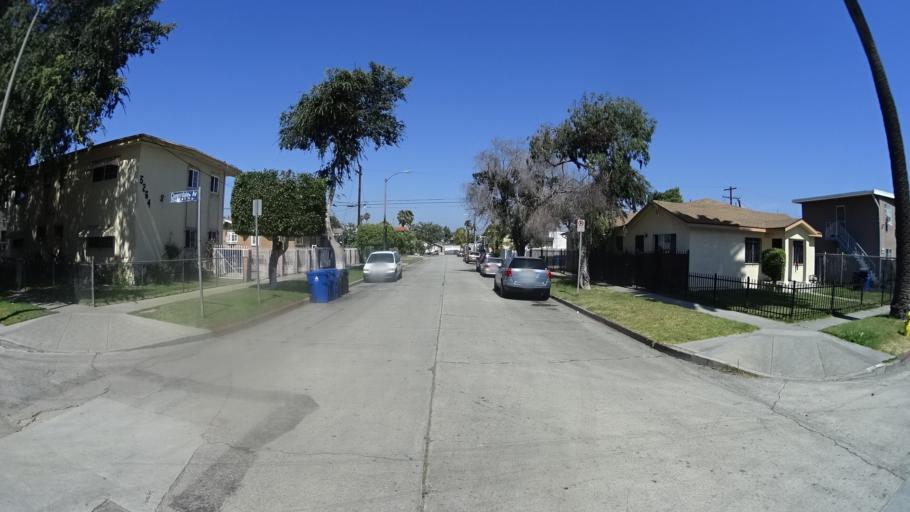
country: US
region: California
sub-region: Los Angeles County
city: View Park-Windsor Hills
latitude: 34.0286
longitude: -118.3589
